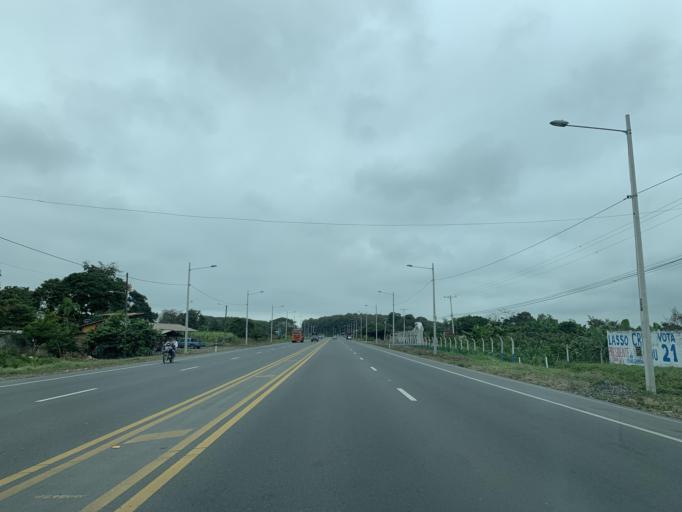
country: EC
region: Guayas
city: Coronel Marcelino Mariduena
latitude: -2.3212
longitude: -79.4616
